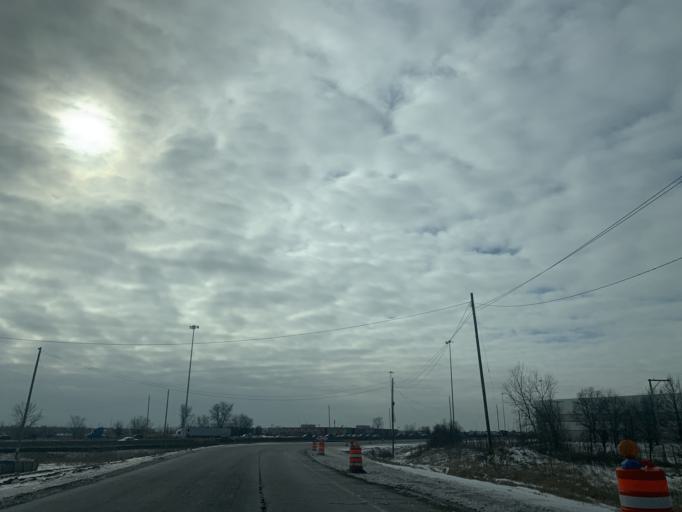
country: US
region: Illinois
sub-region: Will County
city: Romeoville
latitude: 41.6558
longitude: -88.1270
